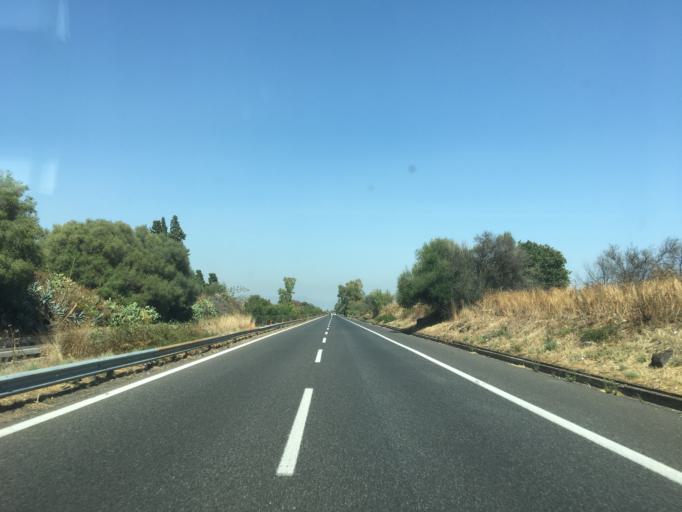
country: IT
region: Sicily
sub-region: Catania
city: Linera
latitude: 37.6439
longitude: 15.1466
